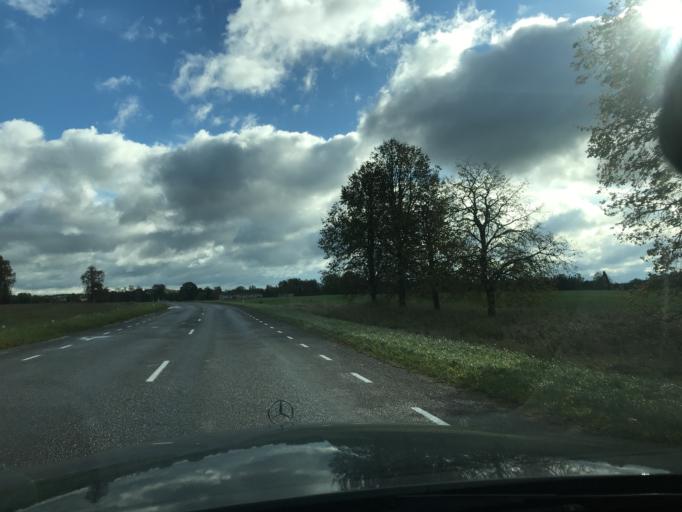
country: EE
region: Valgamaa
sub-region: Torva linn
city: Torva
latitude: 57.9784
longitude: 25.9753
